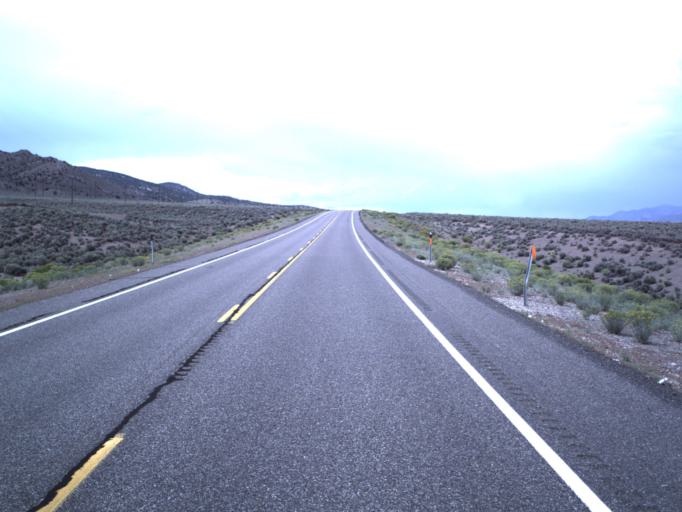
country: US
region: Utah
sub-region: Piute County
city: Junction
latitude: 38.2902
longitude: -112.2253
